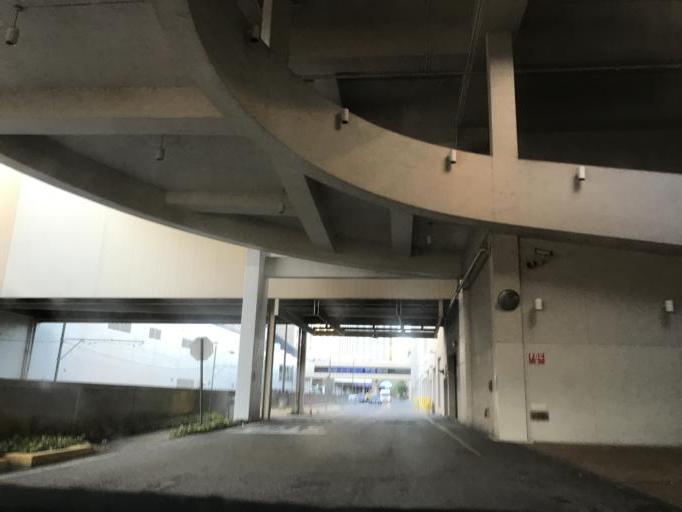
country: US
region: Louisiana
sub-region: Orleans Parish
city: New Orleans
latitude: 29.9462
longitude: -90.0628
